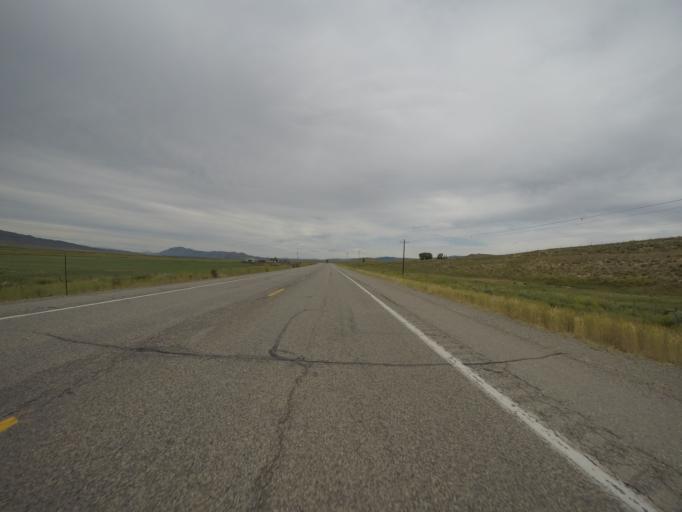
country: US
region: Utah
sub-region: Rich County
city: Randolph
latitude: 41.9961
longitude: -110.9385
